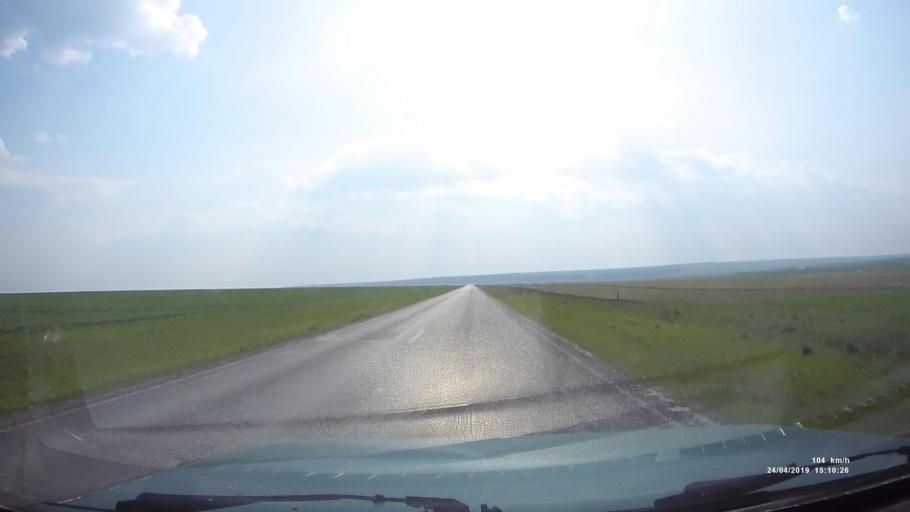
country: RU
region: Rostov
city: Remontnoye
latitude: 46.5498
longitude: 43.3415
